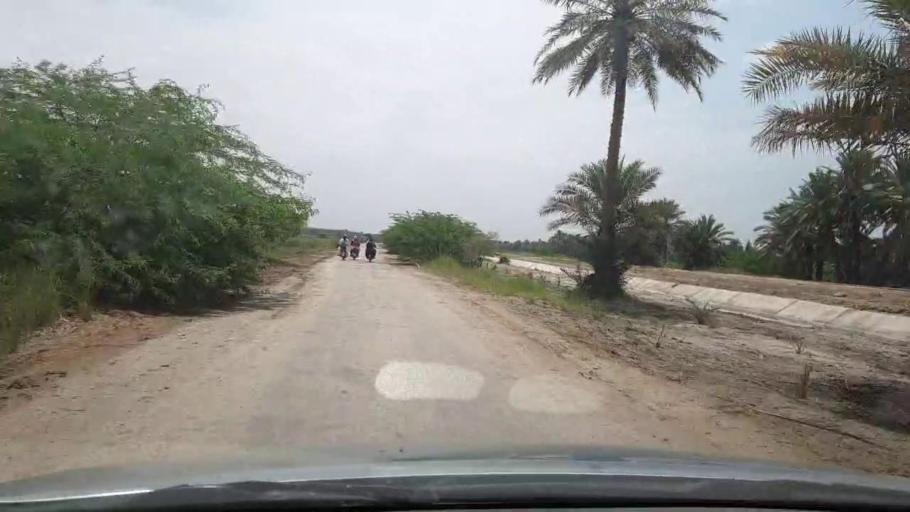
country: PK
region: Sindh
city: Khairpur
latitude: 27.4257
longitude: 68.7808
